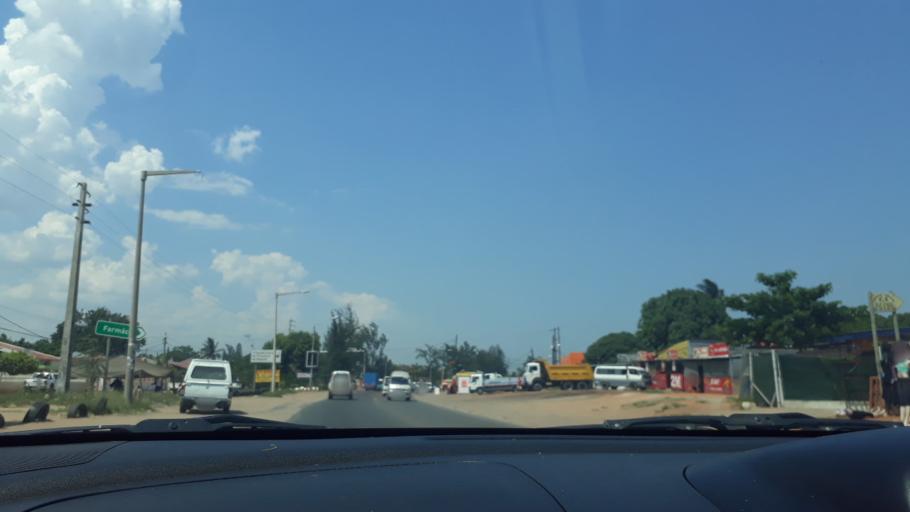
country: MZ
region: Maputo
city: Matola
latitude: -25.9585
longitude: 32.4514
